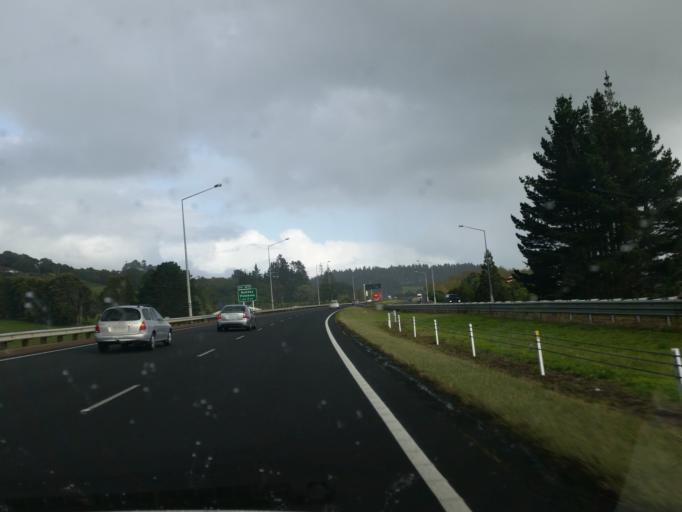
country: NZ
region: Auckland
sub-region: Auckland
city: Pukekohe East
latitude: -37.1727
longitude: 174.9842
